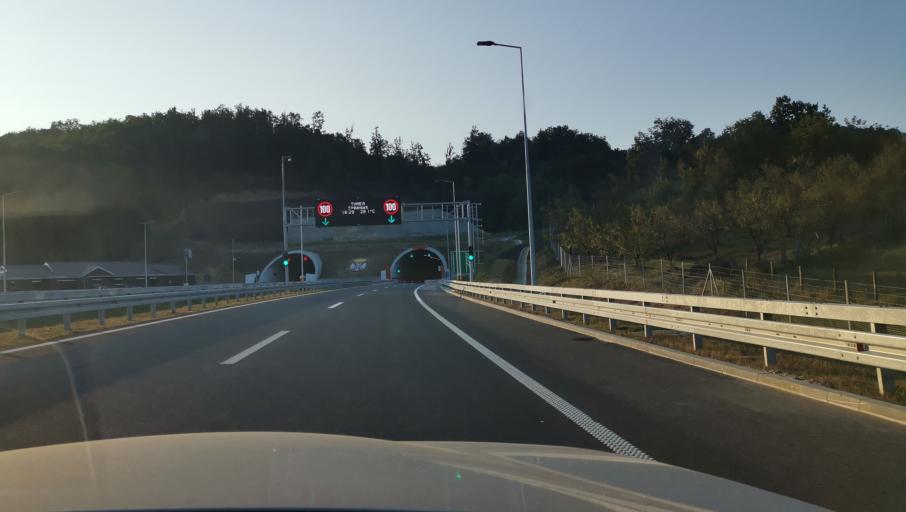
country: RS
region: Central Serbia
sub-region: Kolubarski Okrug
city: Ljig
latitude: 44.2019
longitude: 20.2671
